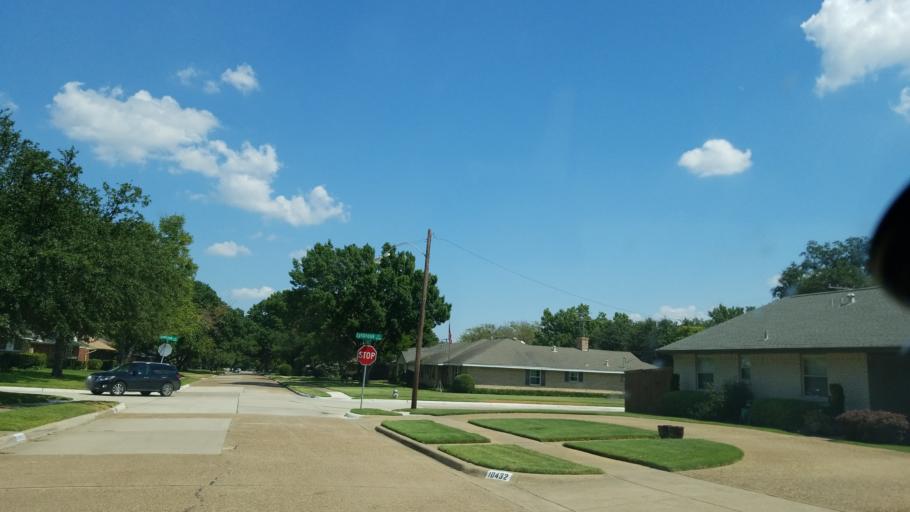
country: US
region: Texas
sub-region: Dallas County
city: Richardson
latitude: 32.8811
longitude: -96.7051
